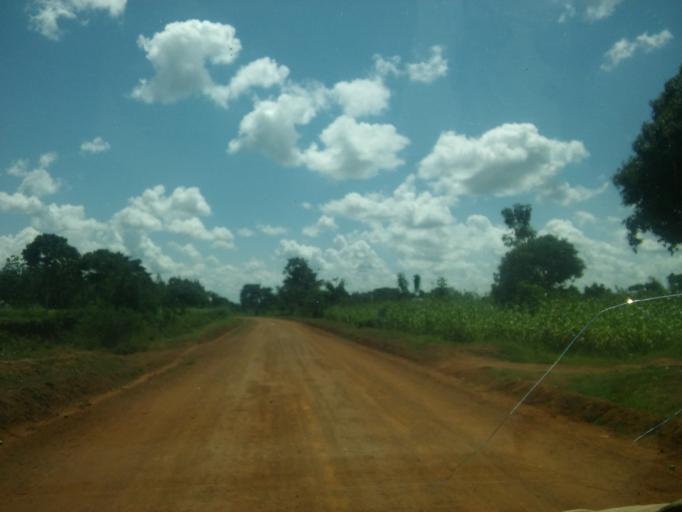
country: UG
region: Eastern Region
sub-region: Budaka District
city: Budaka
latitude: 1.1155
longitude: 33.9452
